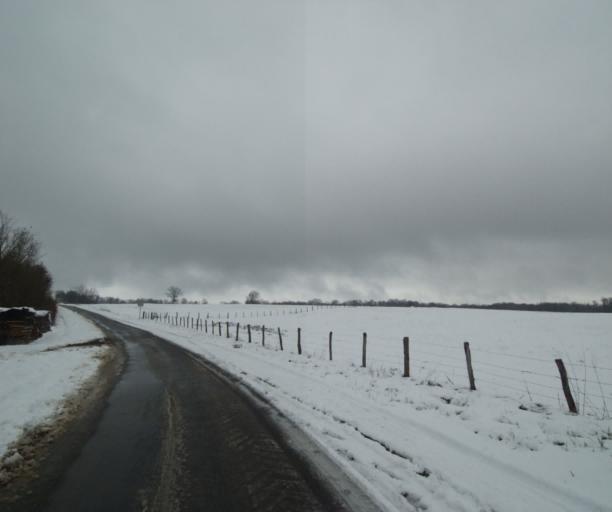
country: FR
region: Champagne-Ardenne
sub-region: Departement de la Haute-Marne
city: Laneuville-a-Remy
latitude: 48.4602
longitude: 4.9204
